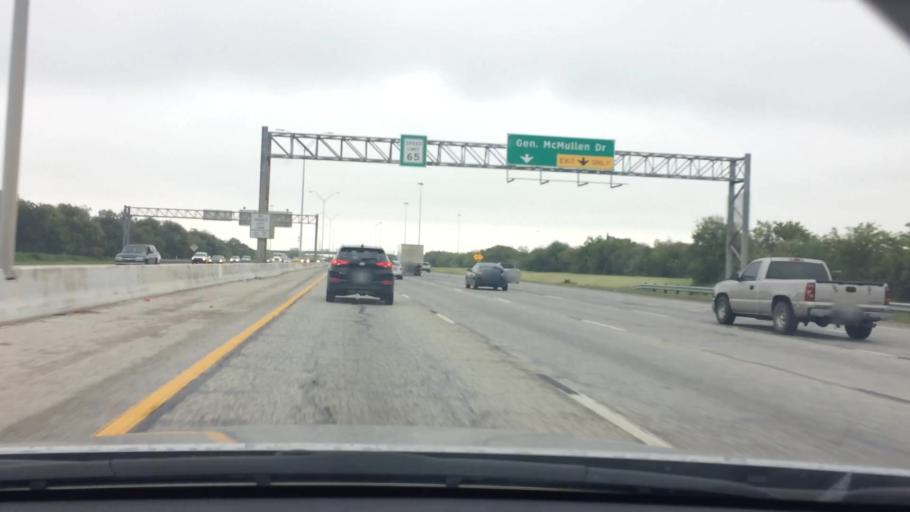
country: US
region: Texas
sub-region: Bexar County
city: Lackland Air Force Base
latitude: 29.4057
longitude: -98.5669
